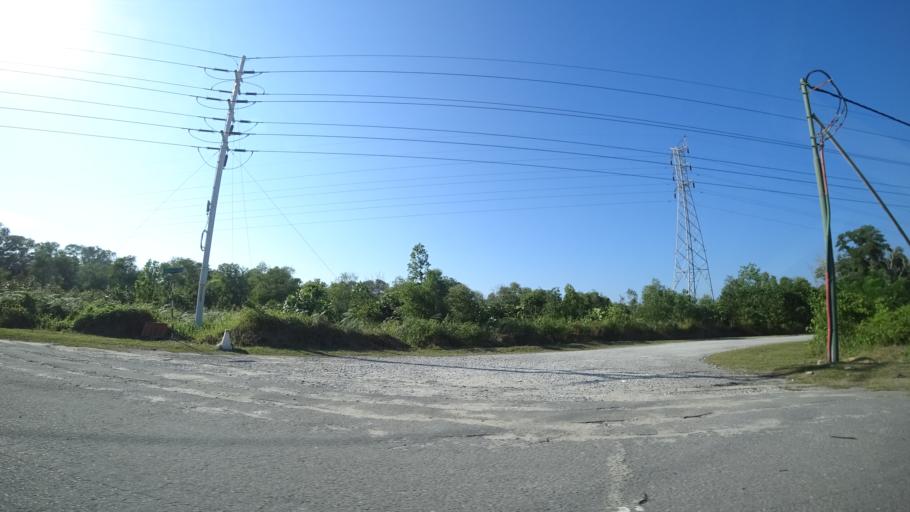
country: BN
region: Tutong
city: Tutong
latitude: 4.7233
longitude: 114.5477
